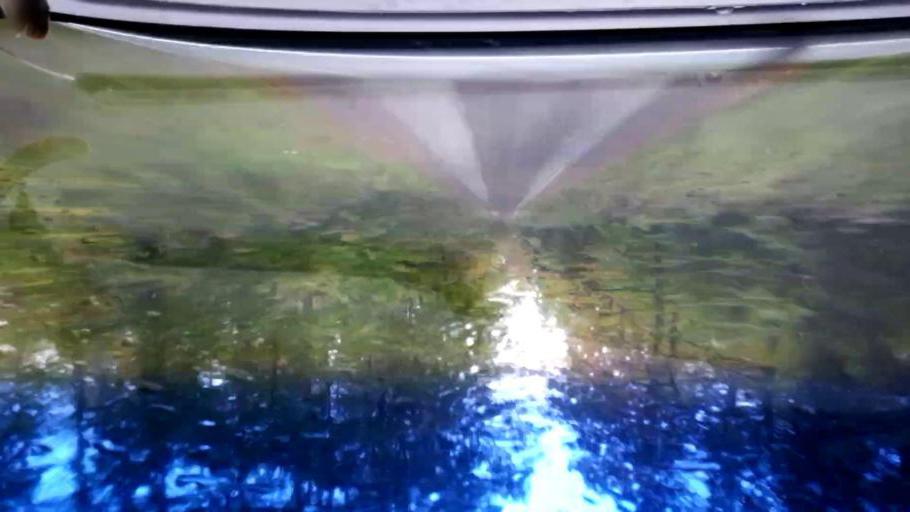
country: DE
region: Bavaria
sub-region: Upper Franconia
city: Burgwindheim
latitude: 49.8563
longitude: 10.6462
